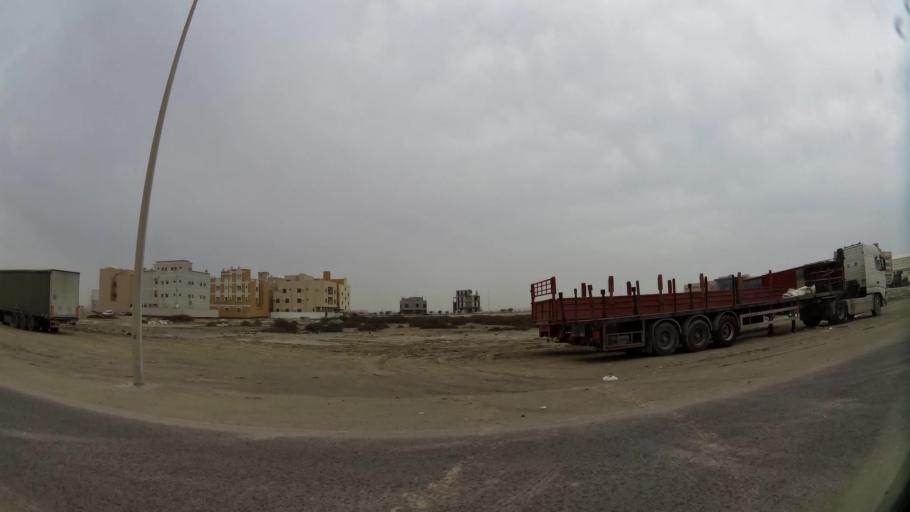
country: BH
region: Northern
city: Madinat `Isa
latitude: 26.1821
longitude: 50.5227
